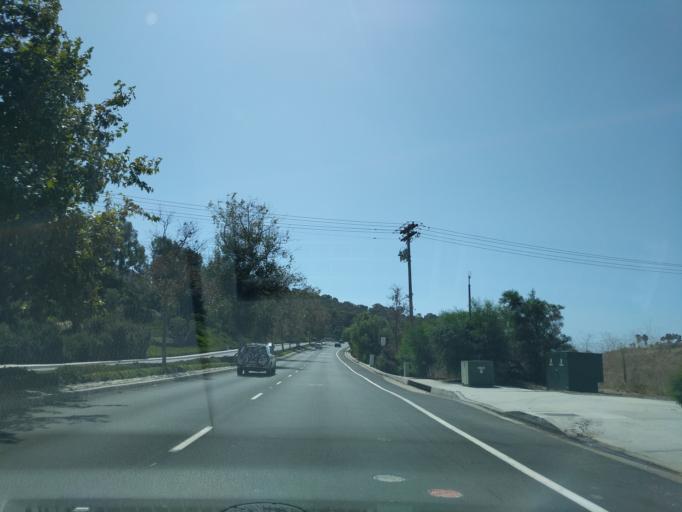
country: US
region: California
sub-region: Orange County
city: Laguna Niguel
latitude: 33.5065
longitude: -117.7079
